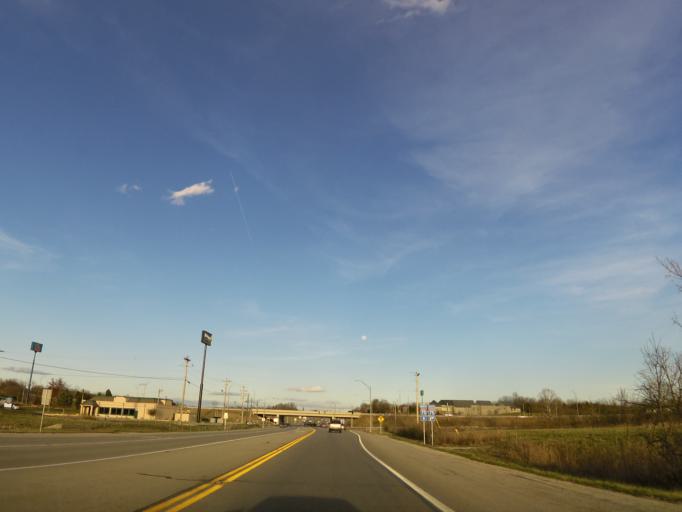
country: US
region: Kentucky
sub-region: Madison County
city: Berea
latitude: 37.5967
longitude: -84.3174
